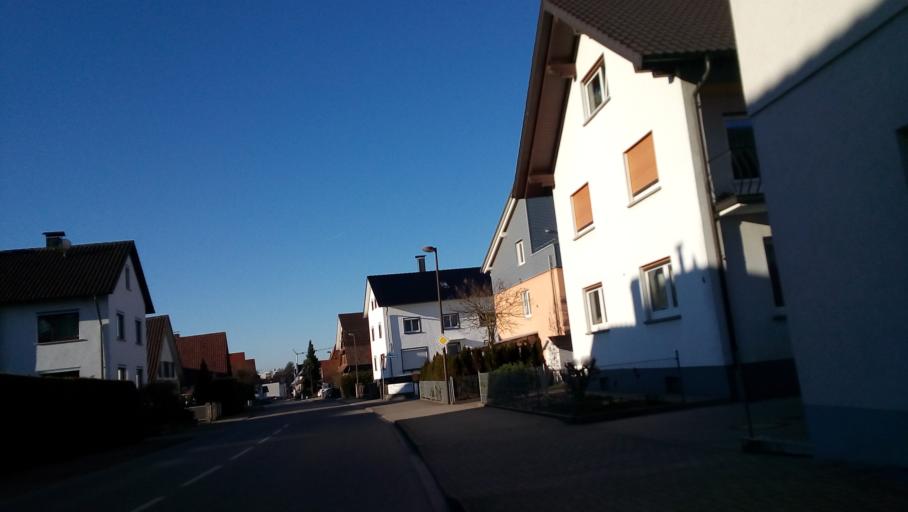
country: DE
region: Baden-Wuerttemberg
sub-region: Freiburg Region
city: Achern
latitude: 48.6198
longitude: 8.0831
